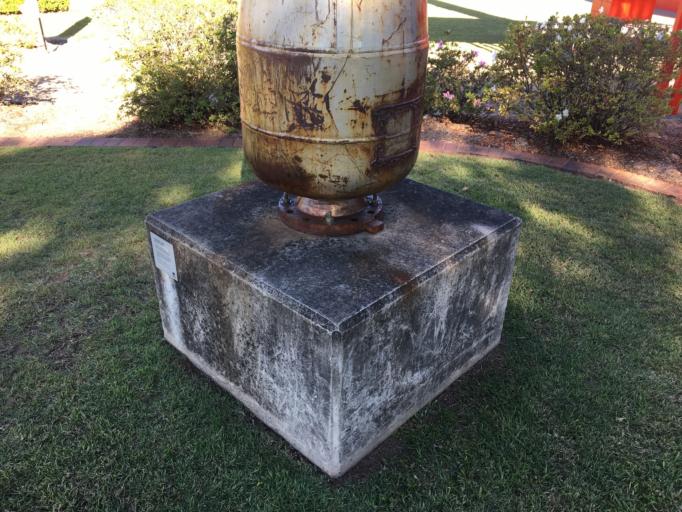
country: AU
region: Queensland
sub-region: Logan
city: Logan City
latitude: -27.6421
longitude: 153.1047
